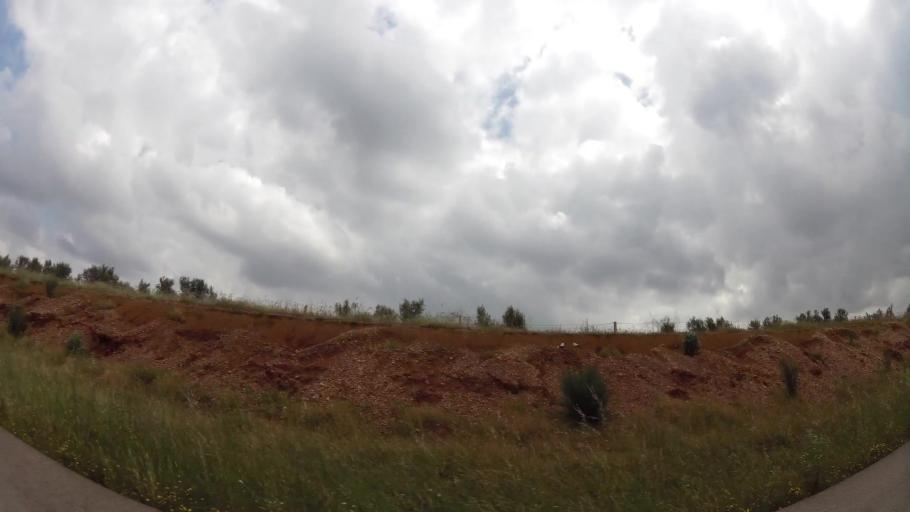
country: MA
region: Rabat-Sale-Zemmour-Zaer
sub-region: Khemisset
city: Tiflet
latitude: 33.9038
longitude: -6.4030
